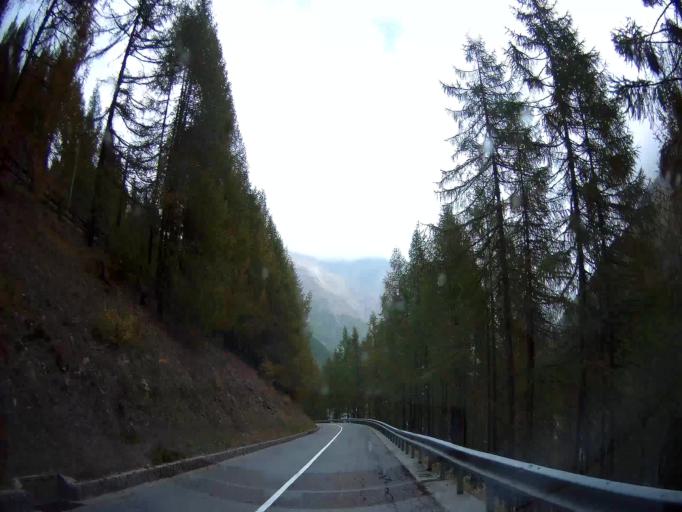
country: IT
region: Trentino-Alto Adige
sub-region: Bolzano
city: Senales
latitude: 46.7351
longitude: 10.8183
